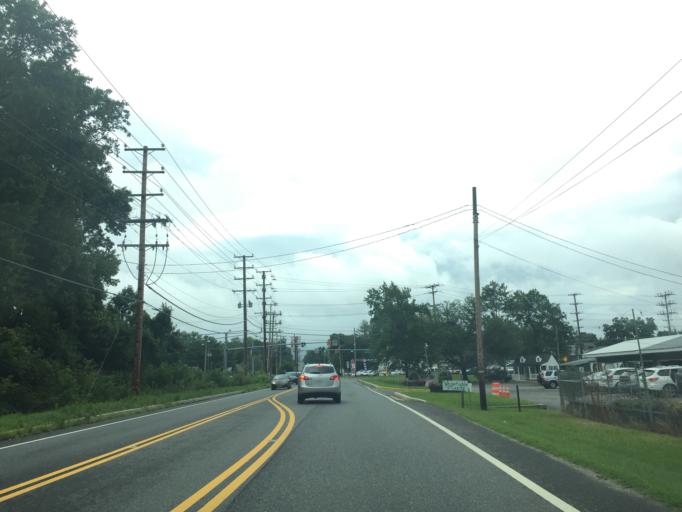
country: US
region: Maryland
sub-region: Harford County
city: Edgewood
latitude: 39.4446
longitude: -76.3108
